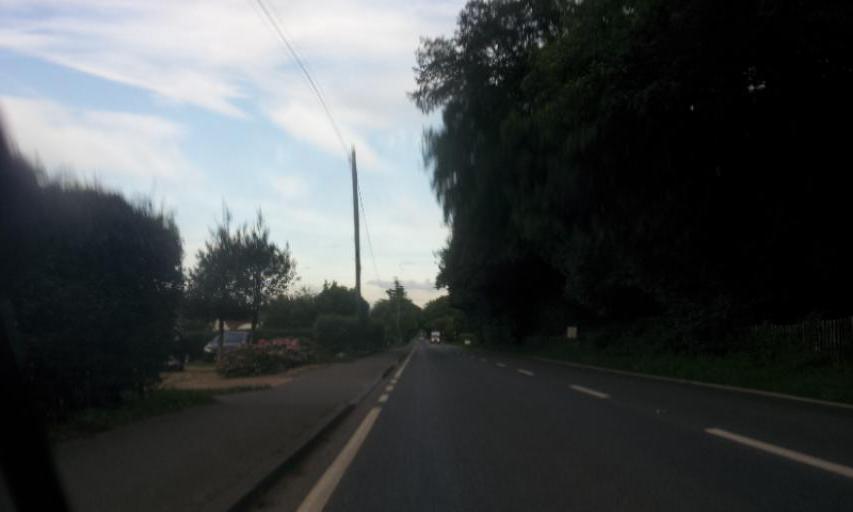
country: GB
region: England
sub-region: Kent
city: Maidstone
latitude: 51.2297
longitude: 0.5239
